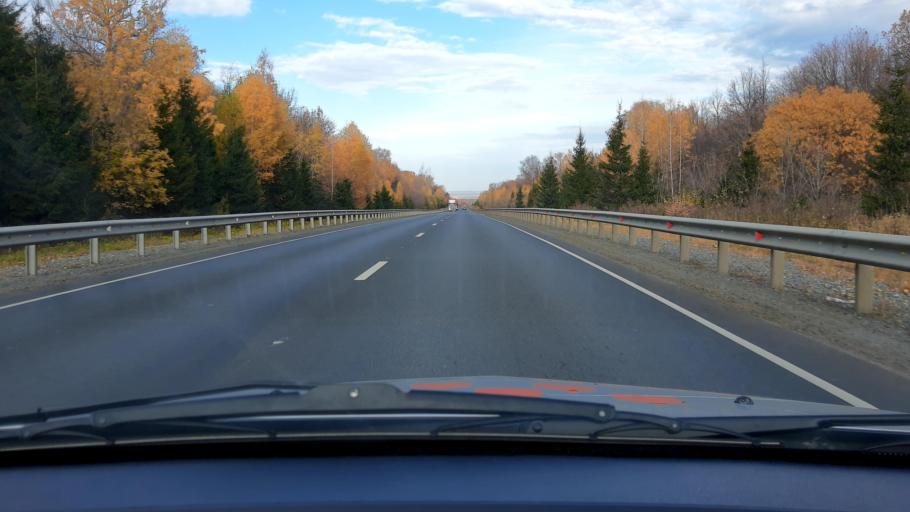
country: RU
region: Bashkortostan
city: Avdon
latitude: 54.8384
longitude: 55.7187
